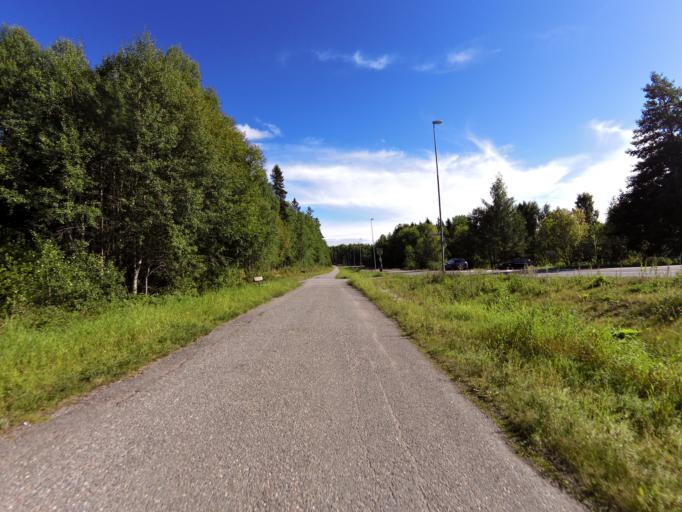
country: SE
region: Gaevleborg
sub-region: Gavle Kommun
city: Gavle
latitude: 60.6653
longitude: 17.1922
